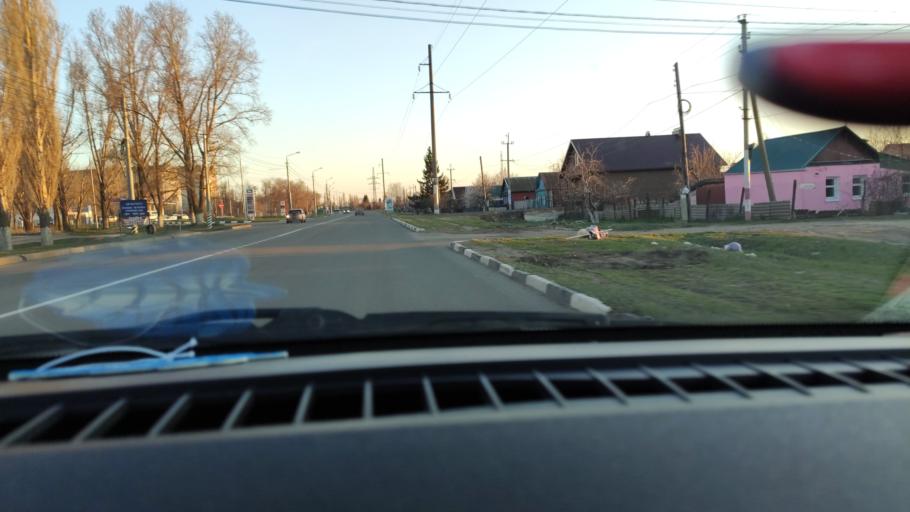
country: RU
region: Saratov
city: Privolzhskiy
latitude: 51.3968
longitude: 46.0341
